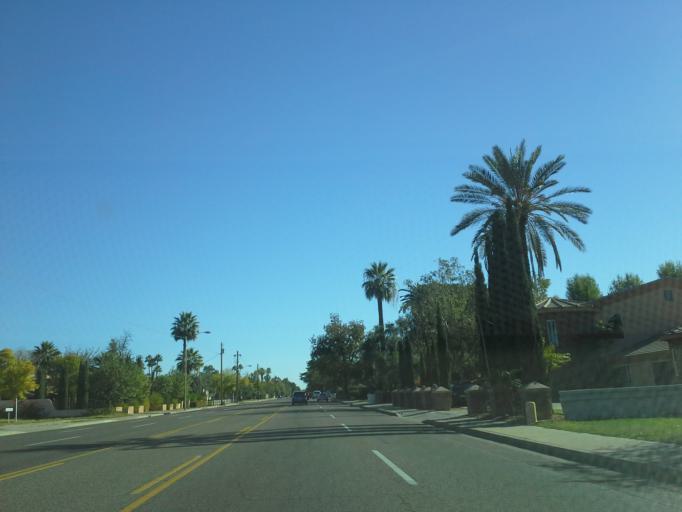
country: US
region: Arizona
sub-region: Maricopa County
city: Phoenix
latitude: 33.5238
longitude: -112.0800
